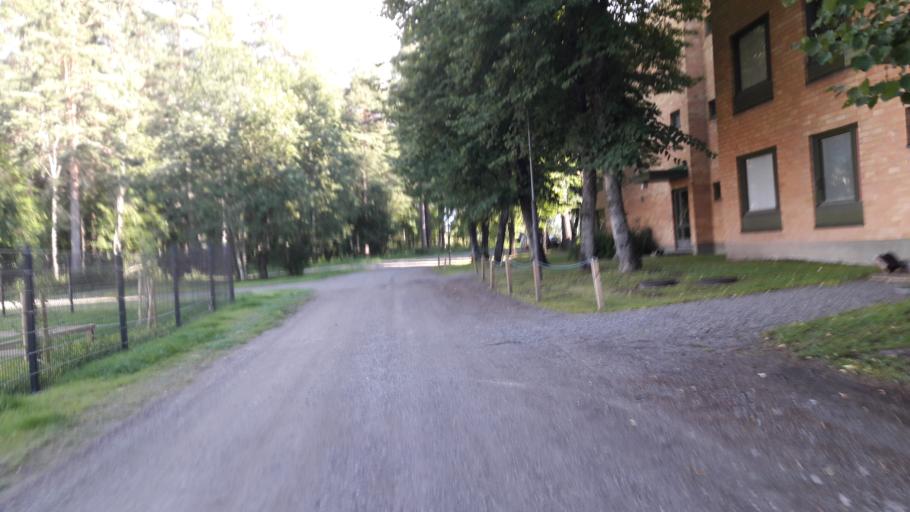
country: FI
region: North Karelia
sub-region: Joensuu
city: Joensuu
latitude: 62.6042
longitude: 29.8014
